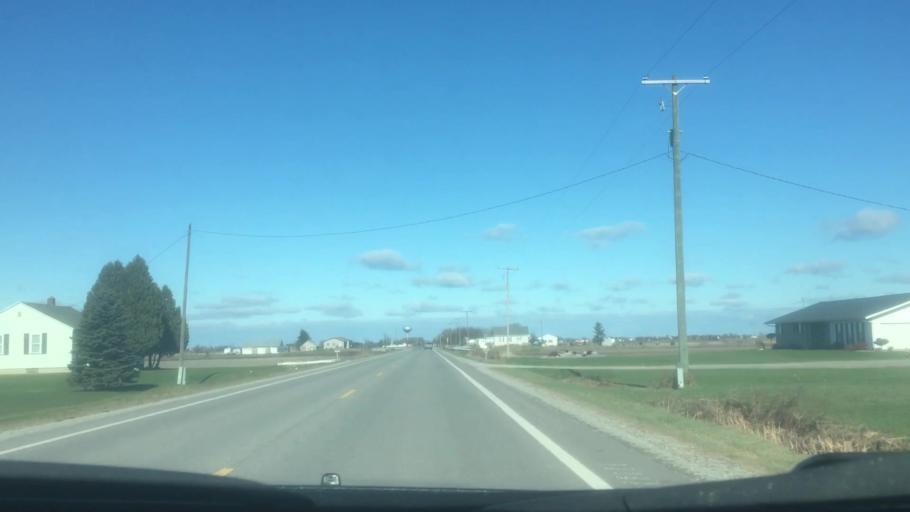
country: US
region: Michigan
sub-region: Bay County
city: Essexville
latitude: 43.5709
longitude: -83.7595
